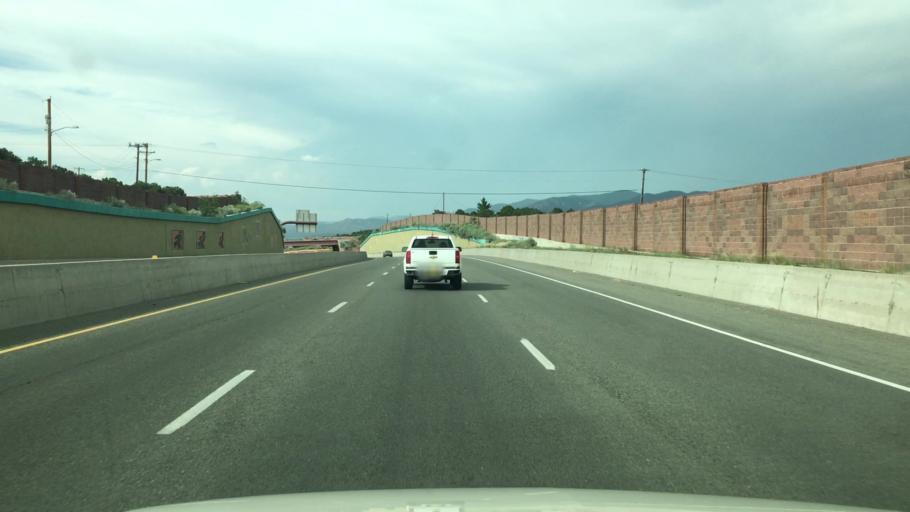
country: US
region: New Mexico
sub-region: Santa Fe County
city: Santa Fe
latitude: 35.7208
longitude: -105.9333
